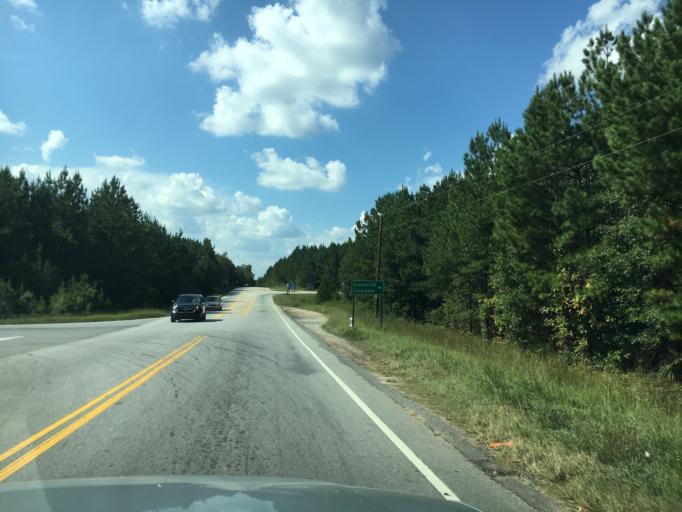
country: US
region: South Carolina
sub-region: Greenville County
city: Fountain Inn
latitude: 34.6393
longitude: -82.1444
